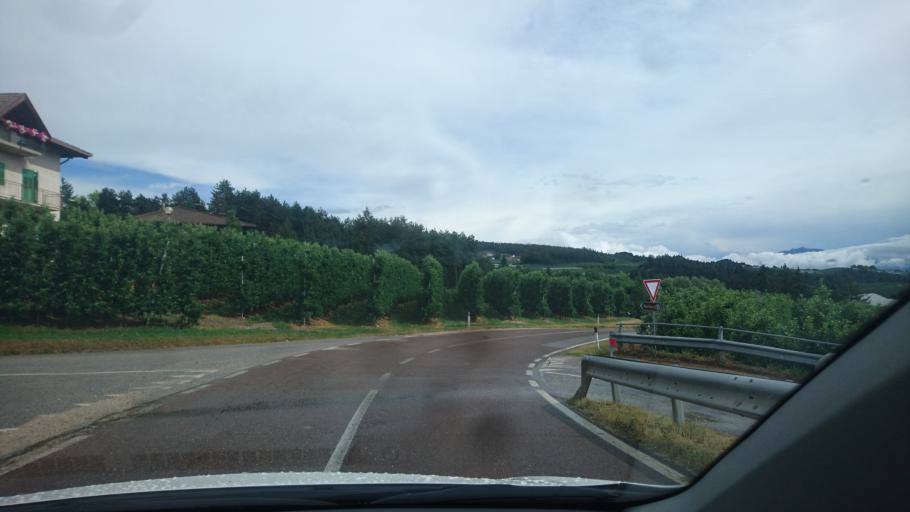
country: IT
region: Trentino-Alto Adige
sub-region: Provincia di Trento
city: Sanzeno
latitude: 46.3756
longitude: 11.0870
